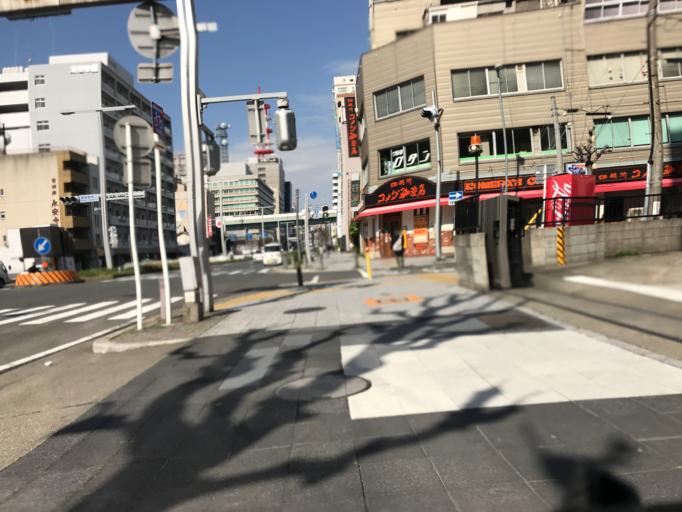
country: JP
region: Aichi
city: Nagoya-shi
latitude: 35.1707
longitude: 136.9172
